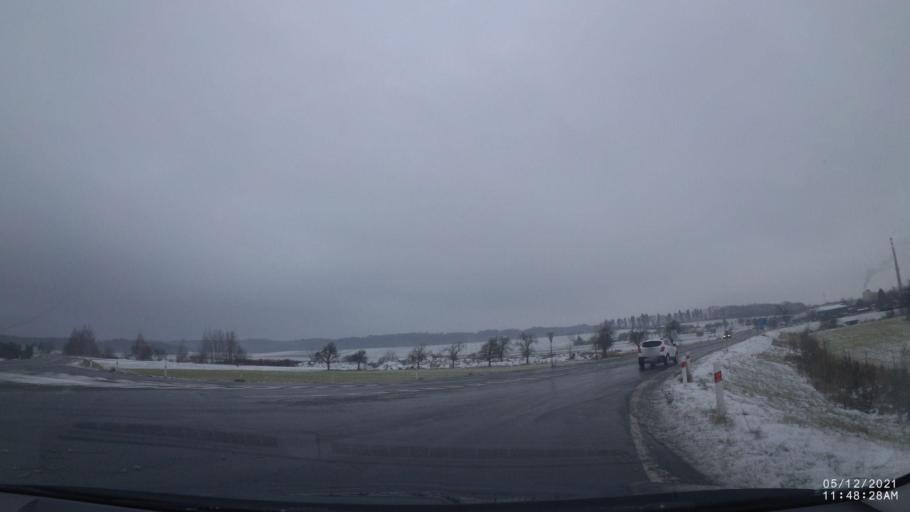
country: CZ
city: Dobruska
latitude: 50.2883
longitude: 16.1694
